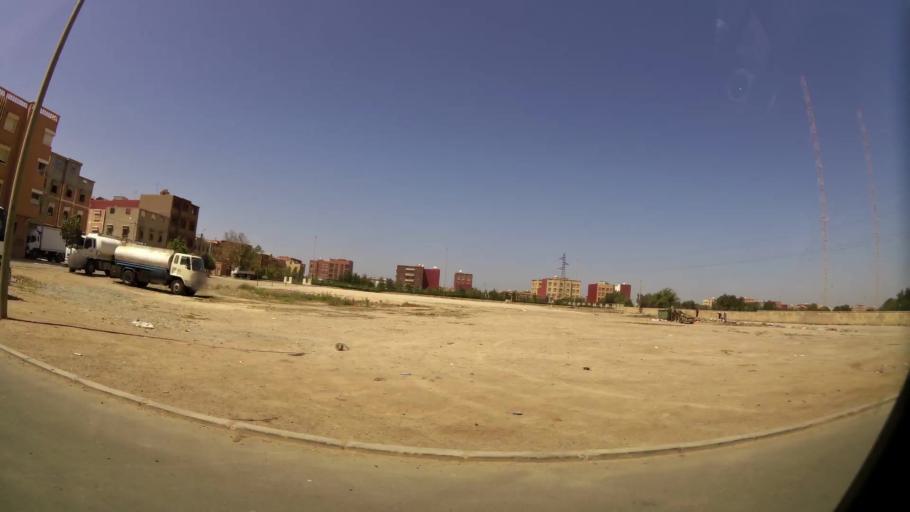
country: MA
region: Souss-Massa-Draa
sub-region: Inezgane-Ait Mellou
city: Inezgane
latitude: 30.3238
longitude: -9.5000
